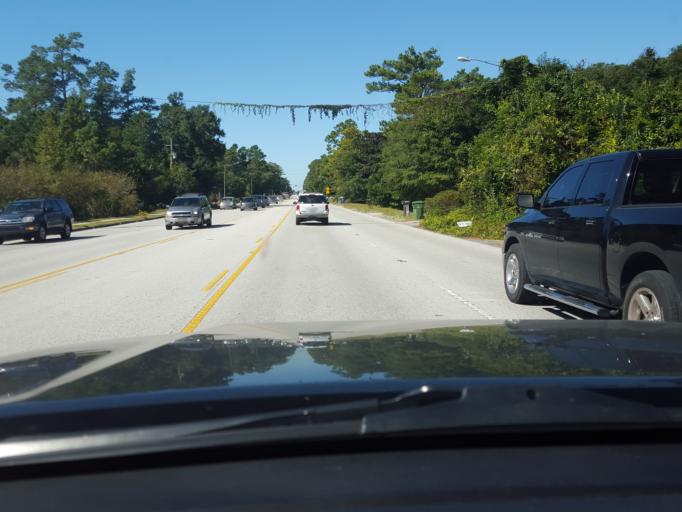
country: US
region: North Carolina
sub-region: New Hanover County
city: Seagate
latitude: 34.2087
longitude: -77.8710
